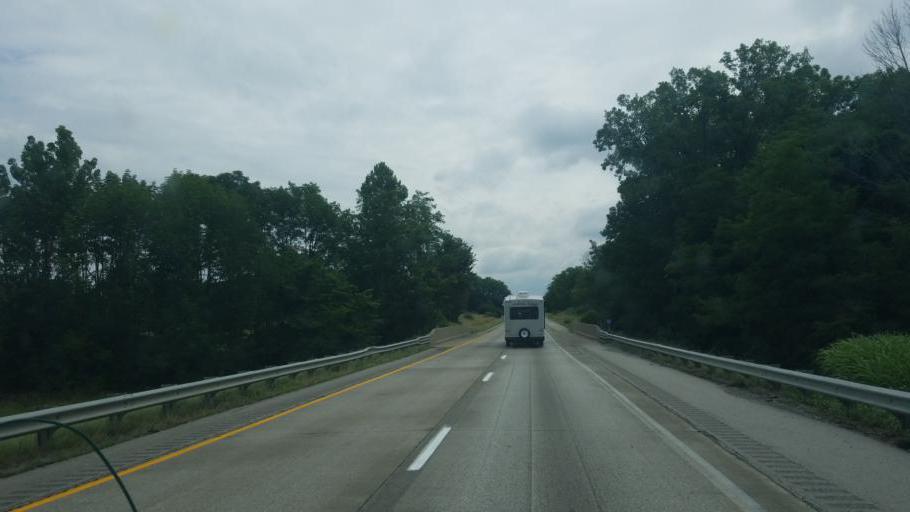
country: US
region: Indiana
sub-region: Morgan County
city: Monrovia
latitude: 39.6301
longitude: -86.4455
